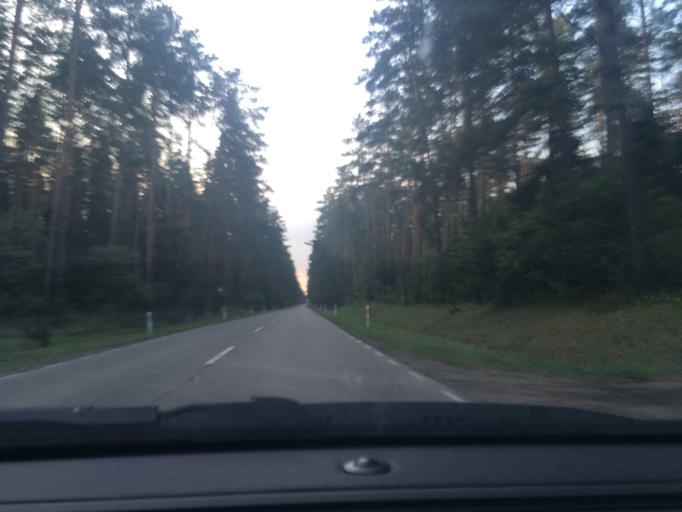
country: PL
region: Podlasie
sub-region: Powiat grajewski
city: Grajewo
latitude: 53.5814
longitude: 22.5265
